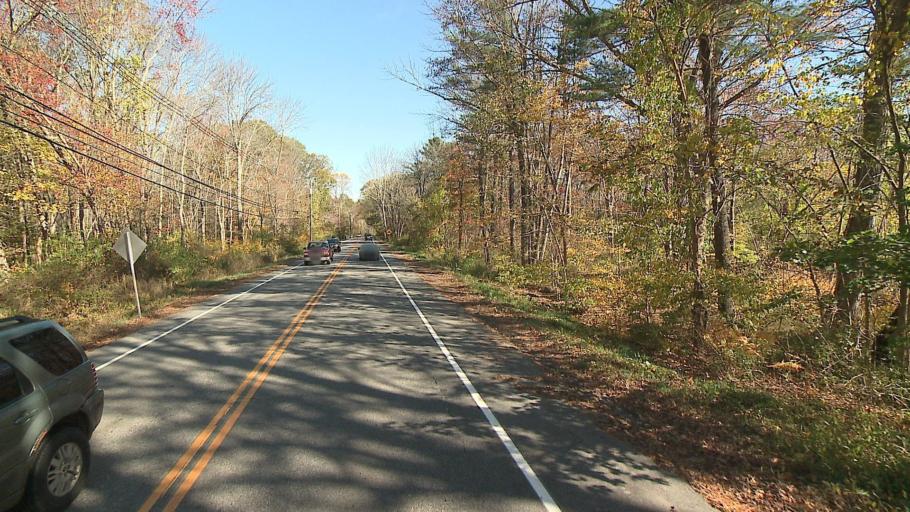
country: US
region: Connecticut
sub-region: Tolland County
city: Storrs
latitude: 41.8311
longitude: -72.2568
